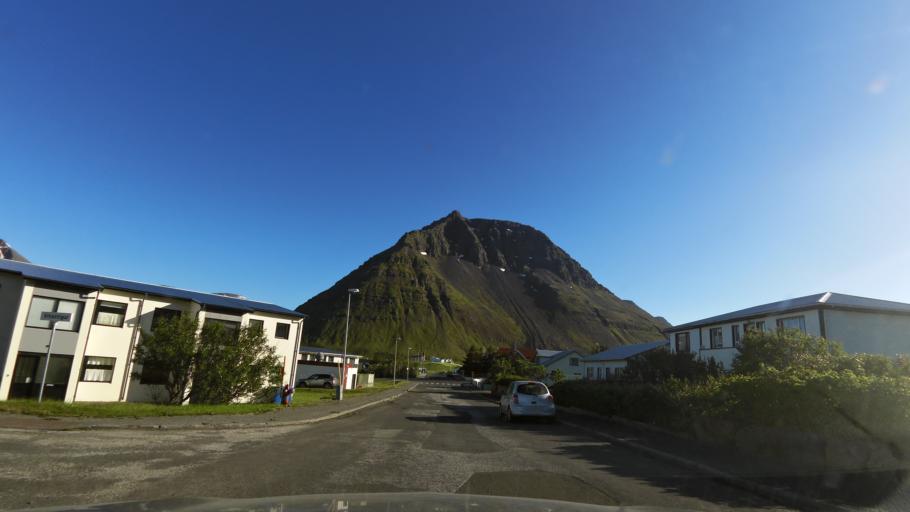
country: IS
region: Westfjords
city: Isafjoerdur
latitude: 66.1585
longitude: -23.2550
